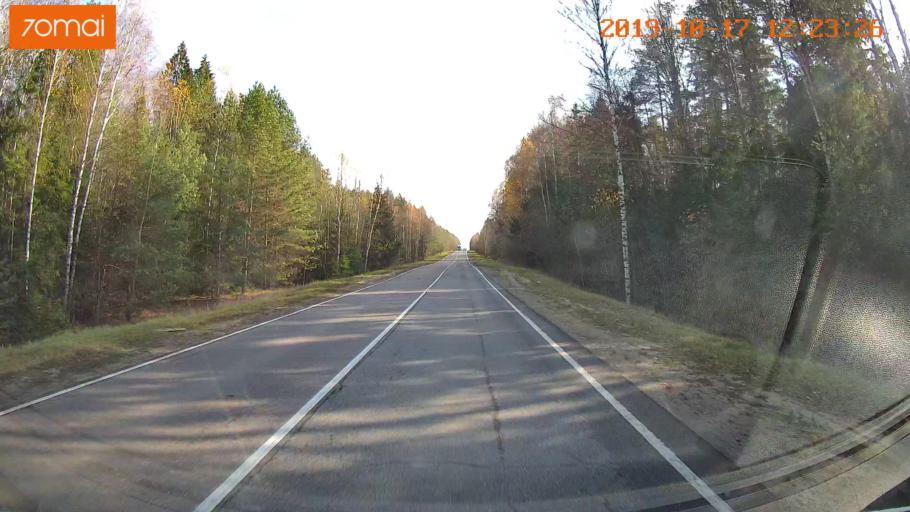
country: RU
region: Rjazan
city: Gus'-Zheleznyy
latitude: 55.0441
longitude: 41.1933
